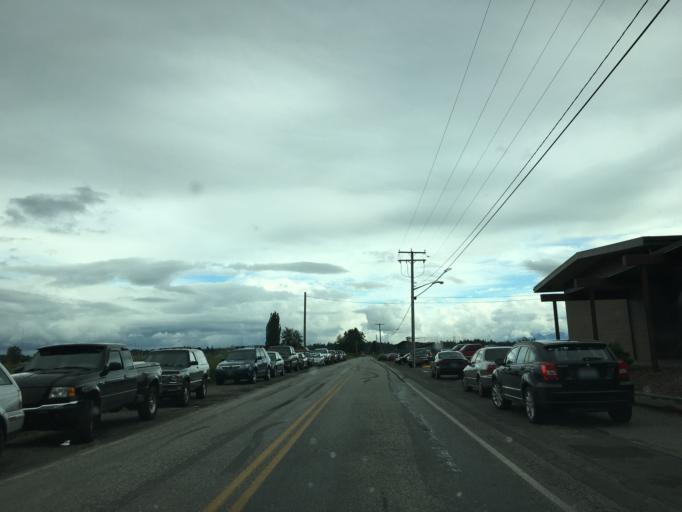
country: US
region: Washington
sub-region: Whatcom County
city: Nooksack
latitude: 48.9649
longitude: -122.3090
